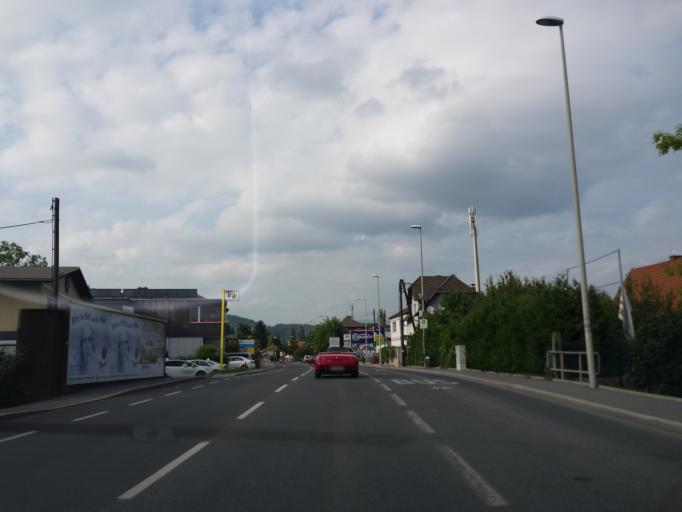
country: AT
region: Styria
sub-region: Graz Stadt
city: Wetzelsdorf
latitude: 47.0582
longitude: 15.3956
